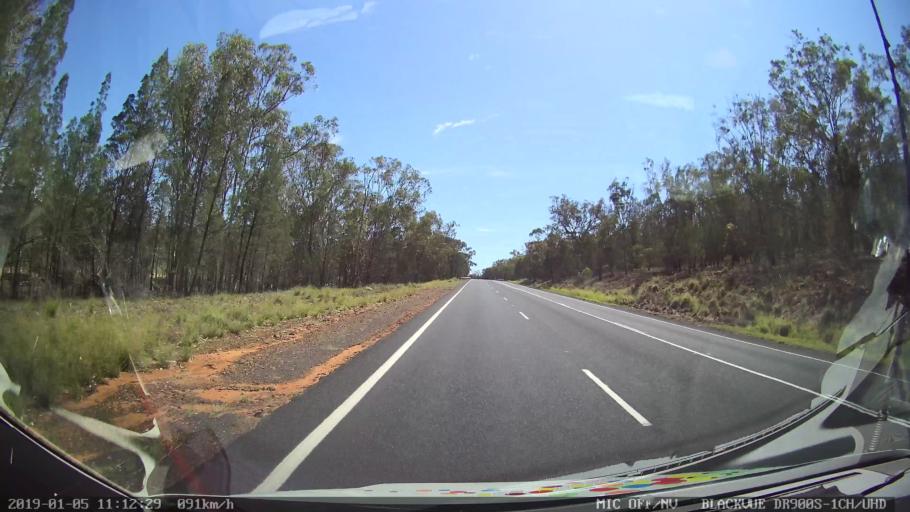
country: AU
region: New South Wales
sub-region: Warrumbungle Shire
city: Coonabarabran
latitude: -31.3816
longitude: 149.2612
